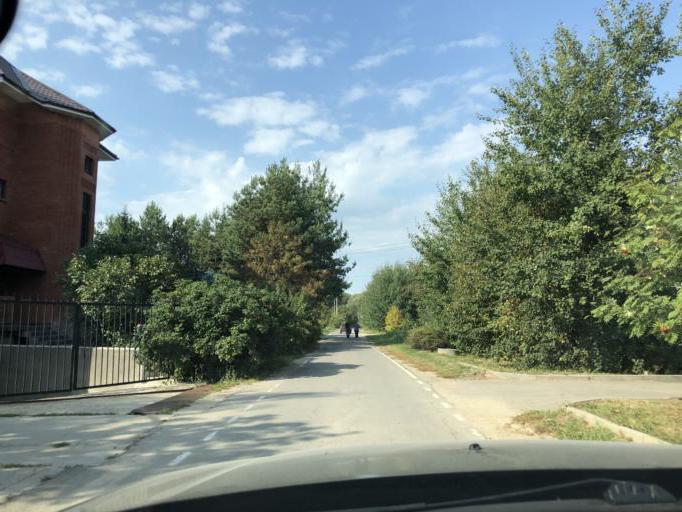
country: RU
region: Moskovskaya
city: L'vovskiy
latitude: 55.3429
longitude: 37.4489
